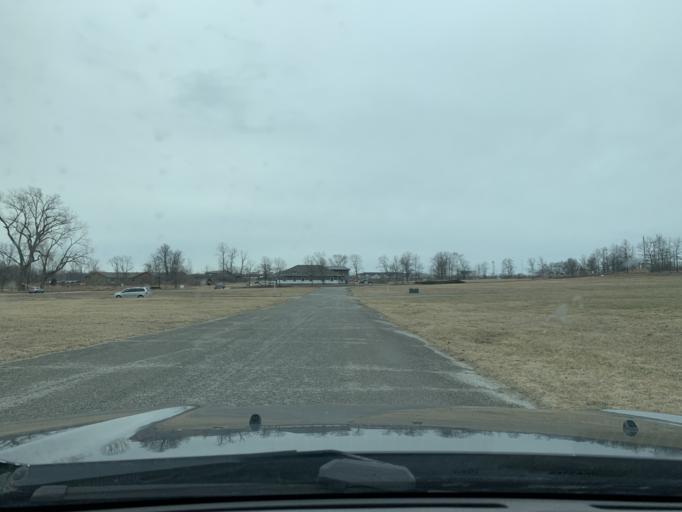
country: US
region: Indiana
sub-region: Porter County
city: Chesterton
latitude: 41.5832
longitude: -87.0431
